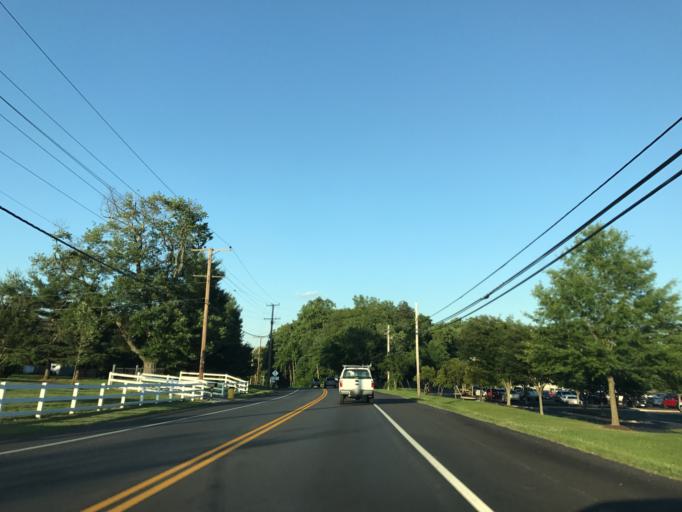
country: US
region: Maryland
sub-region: Anne Arundel County
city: Davidsonville
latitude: 38.9272
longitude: -76.5973
